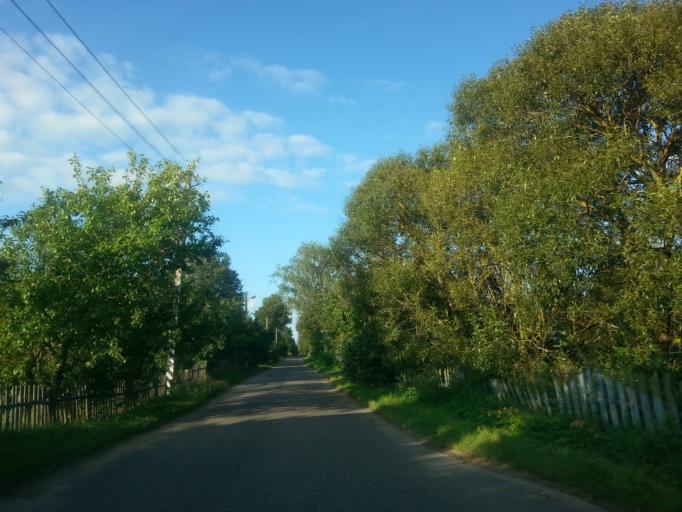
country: BY
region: Minsk
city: Narach
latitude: 54.9733
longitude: 26.6402
